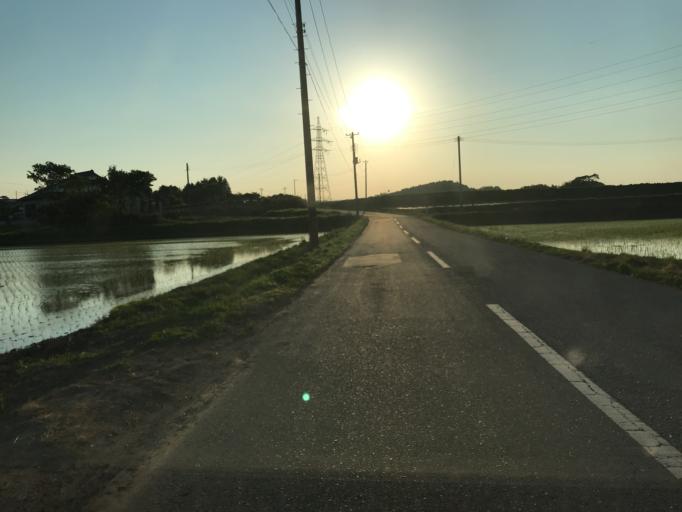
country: JP
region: Fukushima
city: Sukagawa
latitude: 37.1780
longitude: 140.3386
